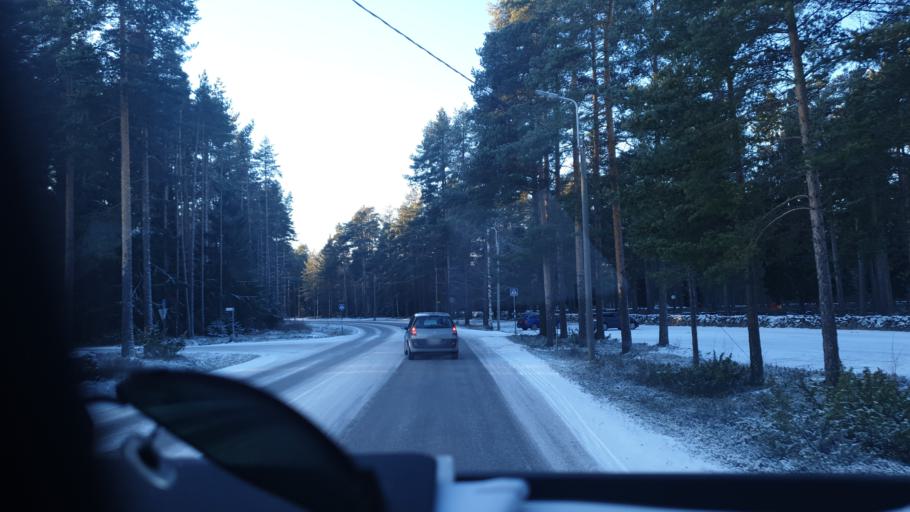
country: FI
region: Central Ostrobothnia
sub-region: Kokkola
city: Kokkola
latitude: 63.8271
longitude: 23.0972
